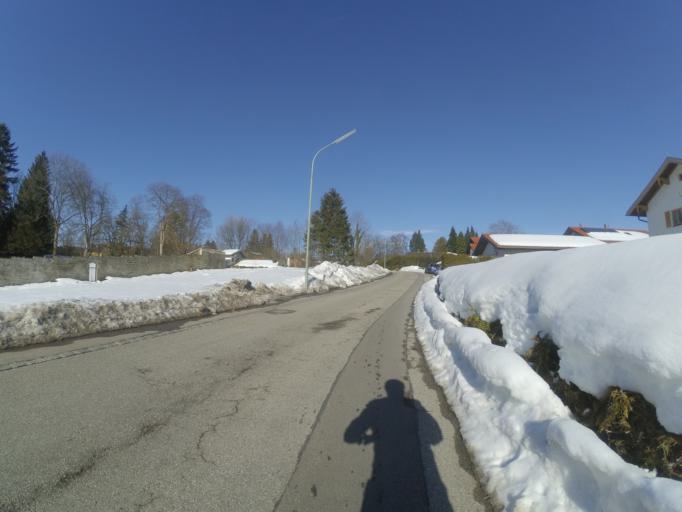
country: DE
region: Bavaria
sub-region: Upper Bavaria
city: Feldkirchen-Westerham
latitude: 47.9142
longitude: 11.8140
